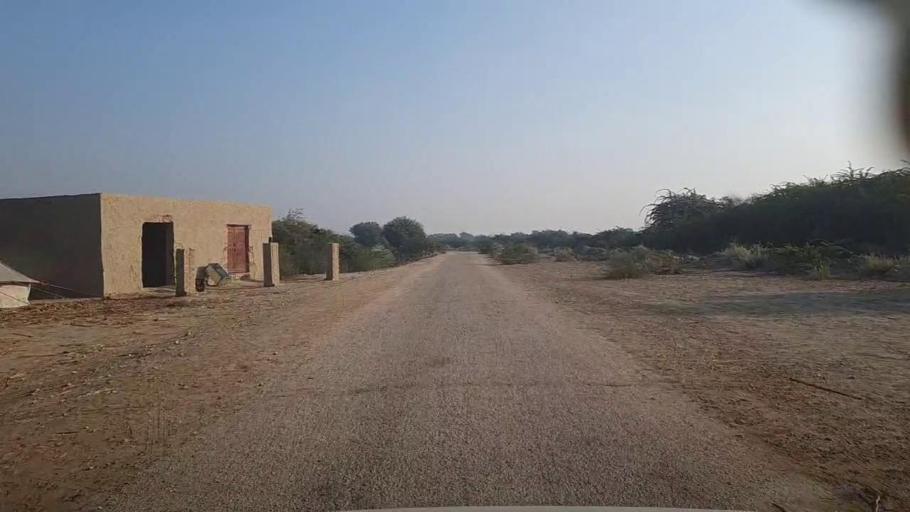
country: PK
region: Sindh
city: Karaundi
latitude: 26.7415
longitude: 68.4775
